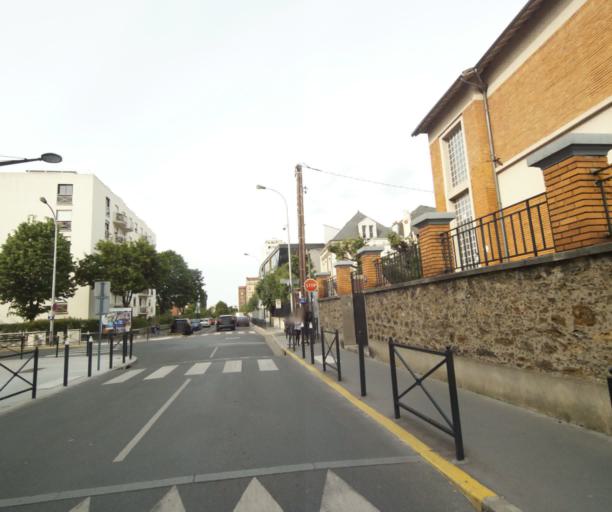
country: FR
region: Ile-de-France
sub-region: Departement des Hauts-de-Seine
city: Bois-Colombes
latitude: 48.9204
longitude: 2.2710
